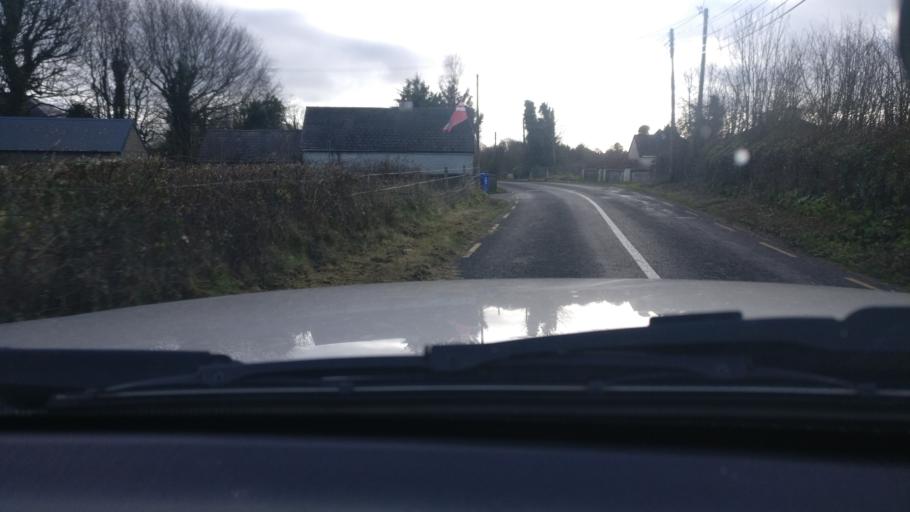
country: IE
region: Connaught
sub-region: County Galway
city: Ballinasloe
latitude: 53.2821
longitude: -8.2420
